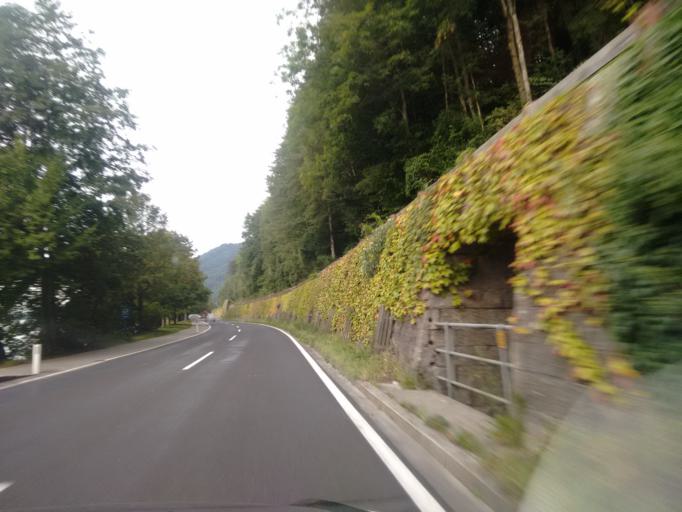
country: AT
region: Upper Austria
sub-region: Politischer Bezirk Vocklabruck
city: Steinbach am Attersee
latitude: 47.8621
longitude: 13.5618
